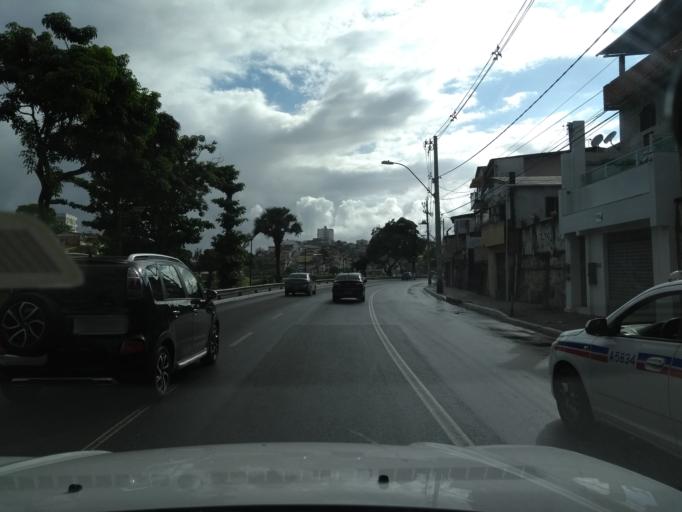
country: BR
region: Bahia
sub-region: Salvador
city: Salvador
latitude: -12.9857
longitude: -38.5068
